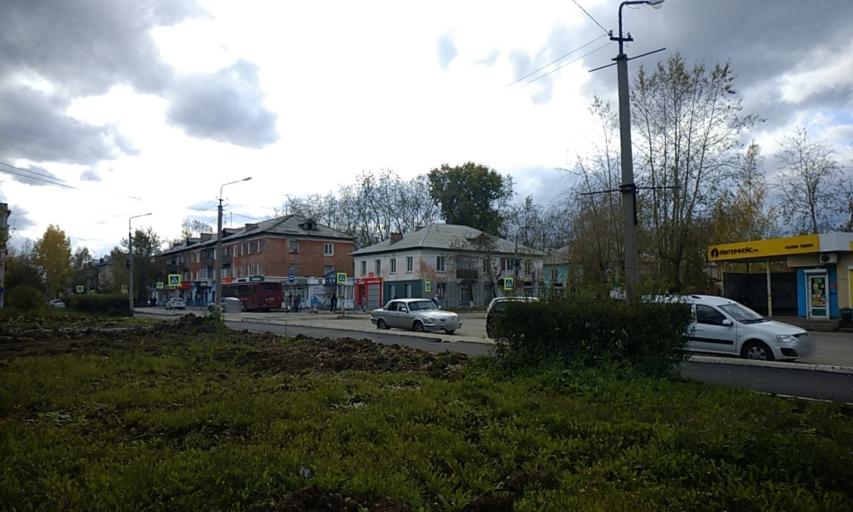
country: RU
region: Sverdlovsk
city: Krasnoural'sk
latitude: 58.3579
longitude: 60.0355
